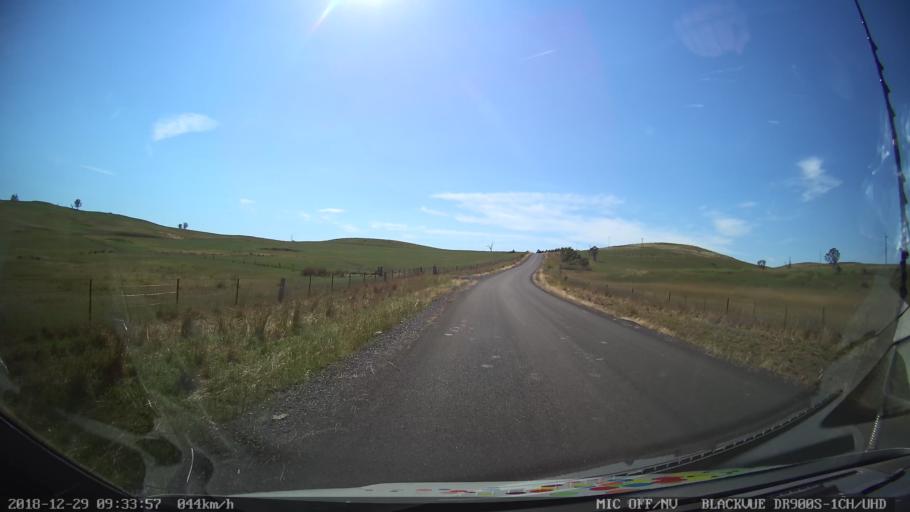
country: AU
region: New South Wales
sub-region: Upper Lachlan Shire
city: Crookwell
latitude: -34.6276
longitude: 149.3467
